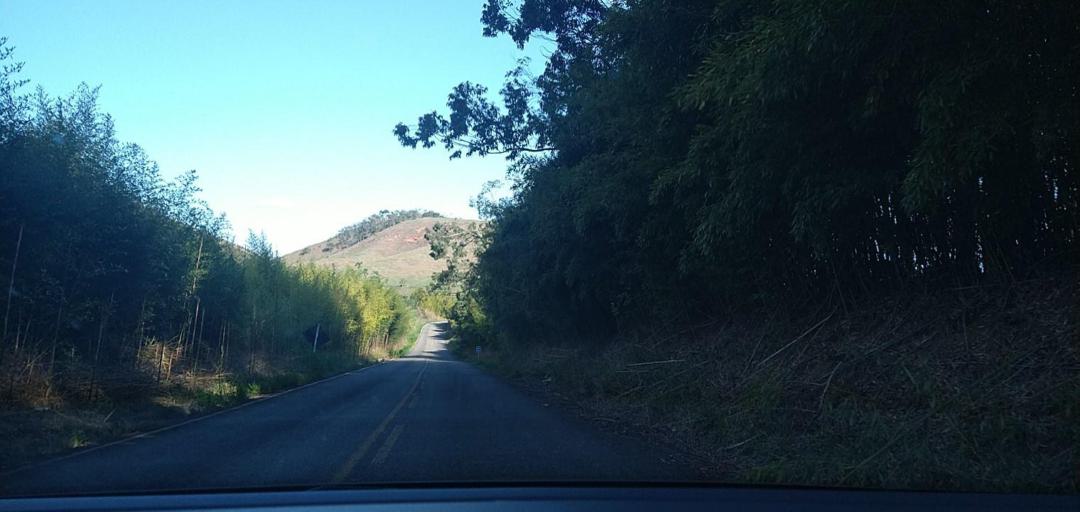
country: BR
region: Minas Gerais
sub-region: Alvinopolis
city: Alvinopolis
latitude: -20.1965
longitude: -42.9303
